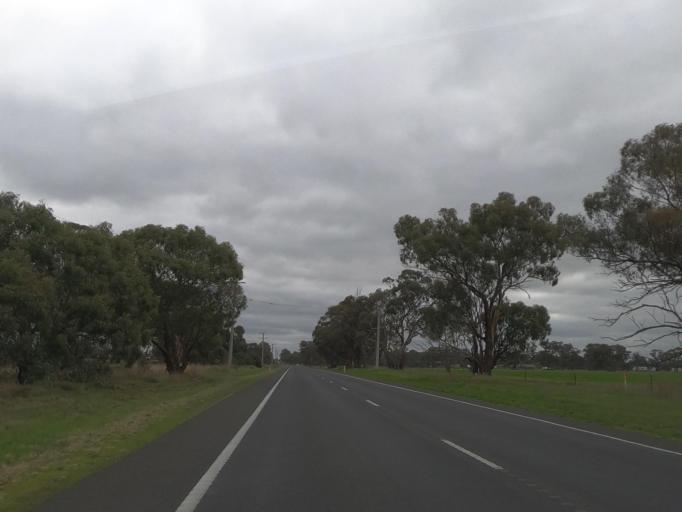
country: AU
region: Victoria
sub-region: Greater Bendigo
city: Long Gully
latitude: -36.6130
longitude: 143.9594
